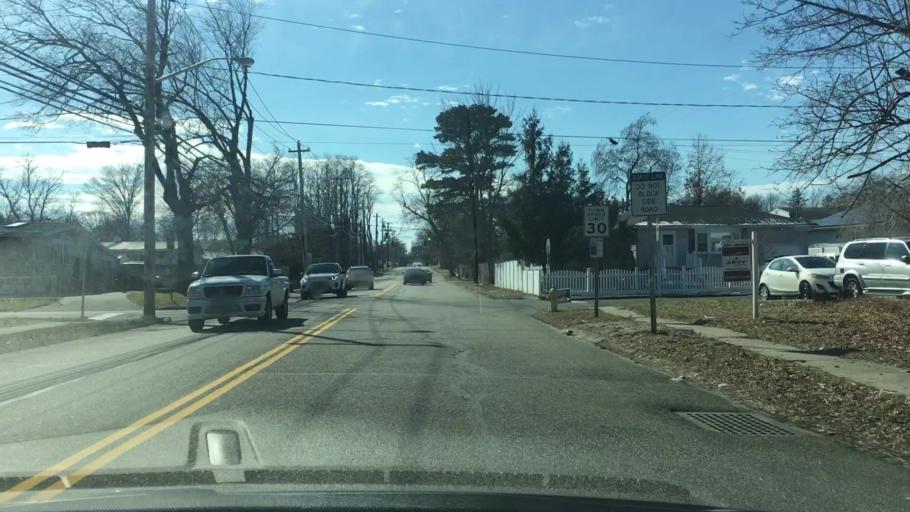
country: US
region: New York
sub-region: Suffolk County
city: West Babylon
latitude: 40.7246
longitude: -73.3465
